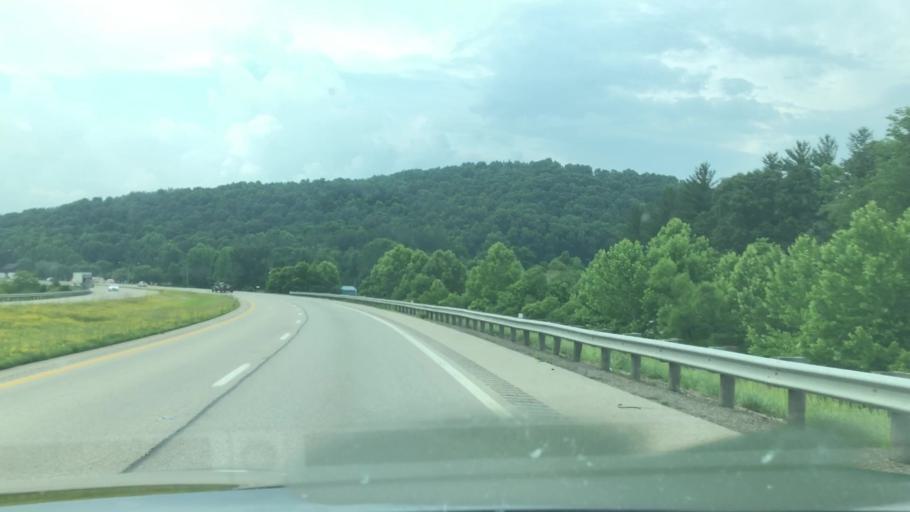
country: US
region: Ohio
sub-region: Jackson County
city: Jackson
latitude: 39.1616
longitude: -82.7336
